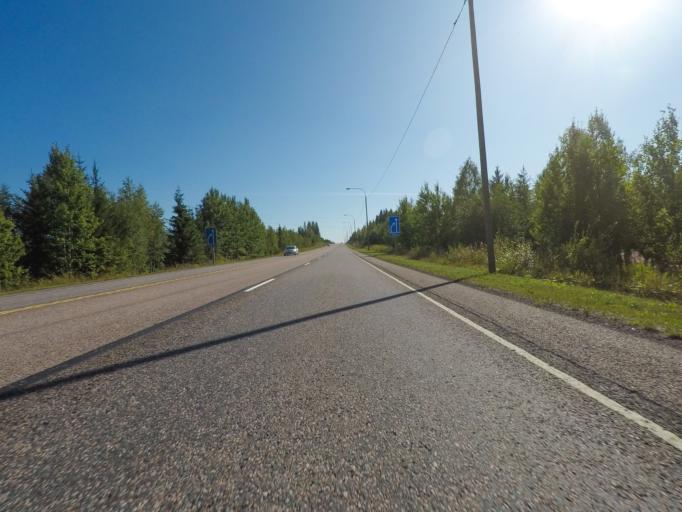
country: FI
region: Northern Savo
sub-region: Varkaus
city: Varkaus
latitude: 62.3753
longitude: 27.8094
